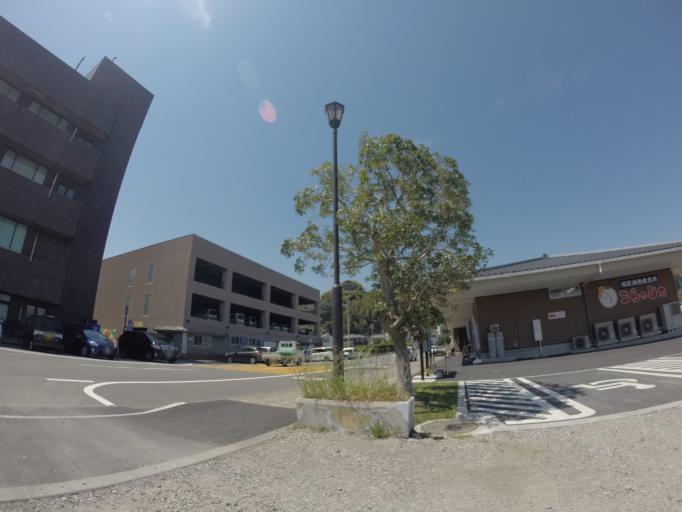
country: JP
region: Shizuoka
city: Shimoda
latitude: 34.7730
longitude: 139.0416
